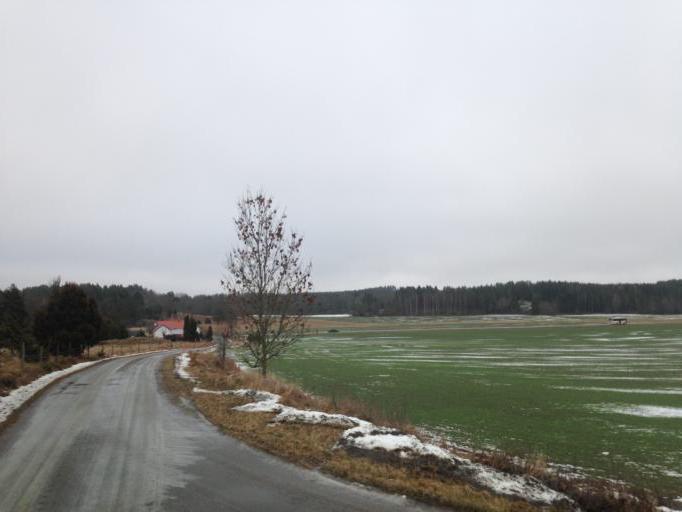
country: SE
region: OEstergoetland
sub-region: Norrkopings Kommun
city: Krokek
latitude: 58.5664
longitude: 16.5878
